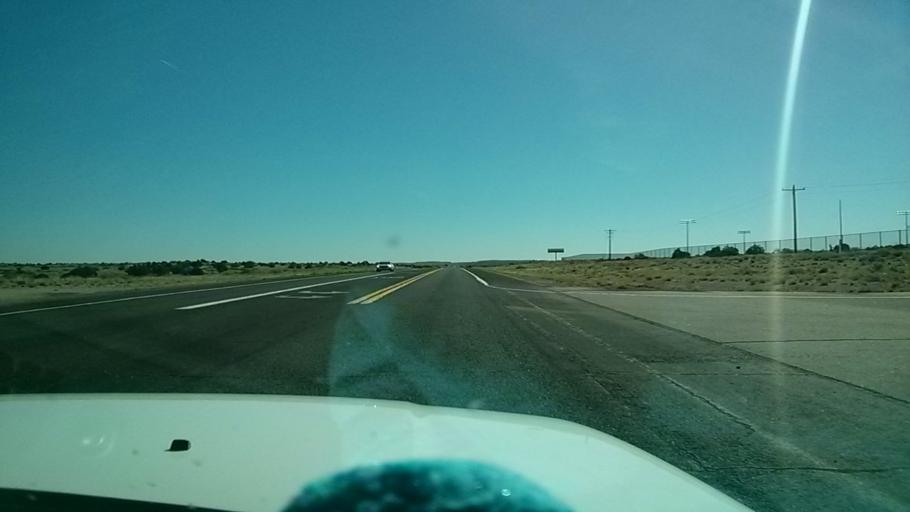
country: US
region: Arizona
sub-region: Mohave County
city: Peach Springs
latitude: 35.5016
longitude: -113.5287
